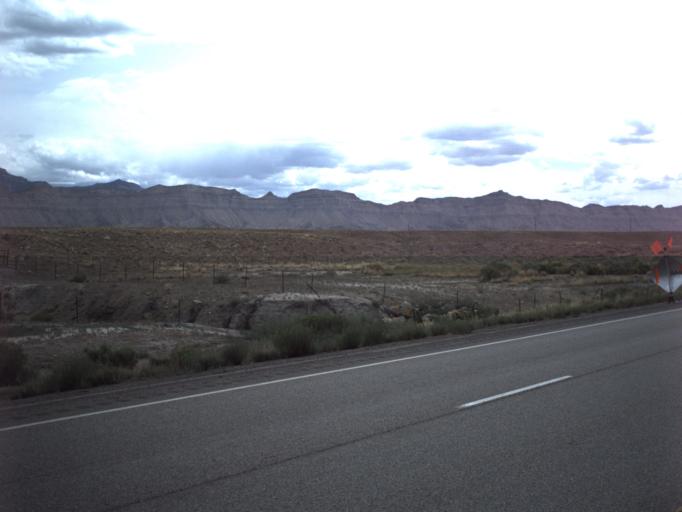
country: US
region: Utah
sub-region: Carbon County
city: East Carbon City
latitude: 39.3766
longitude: -110.4025
